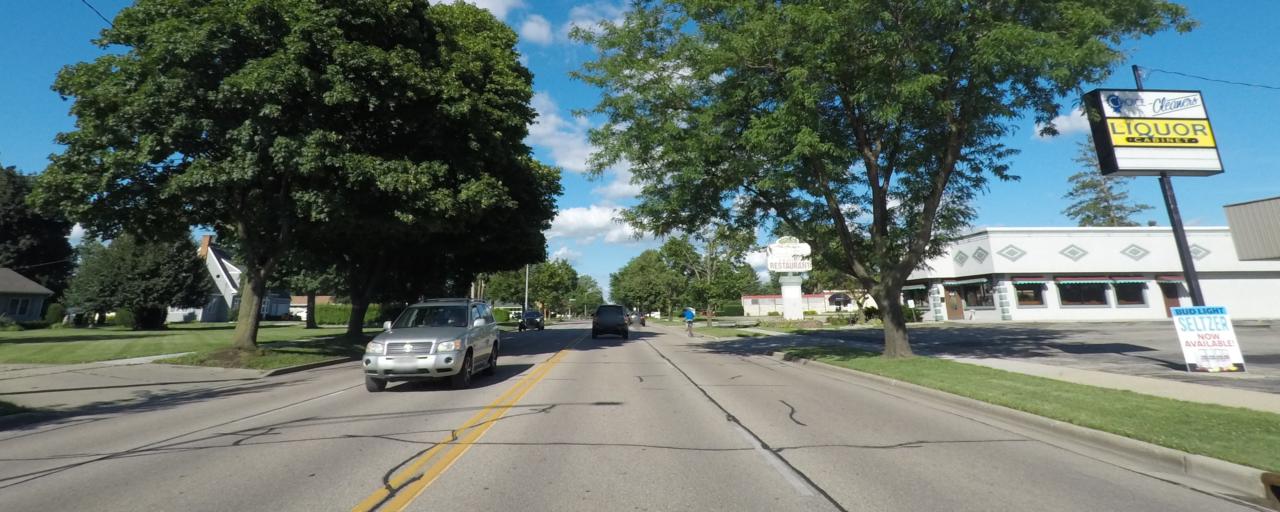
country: US
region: Wisconsin
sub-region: Rock County
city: Janesville
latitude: 42.6923
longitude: -88.9987
